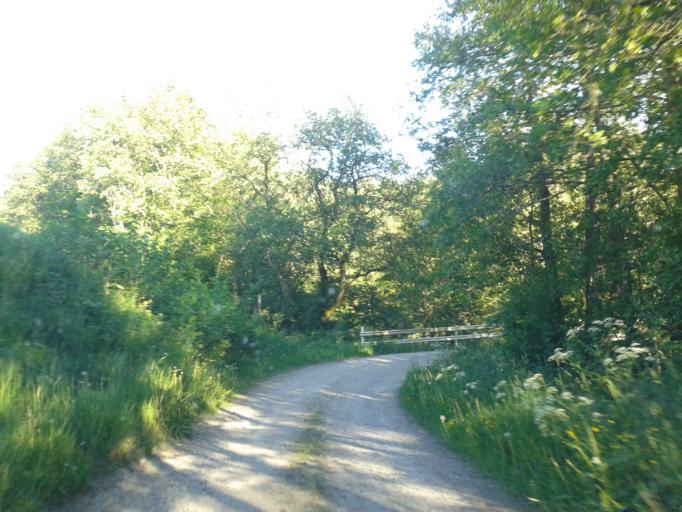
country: SE
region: Vaestra Goetaland
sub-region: Stromstads Kommun
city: Stroemstad
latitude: 58.8976
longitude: 11.3202
